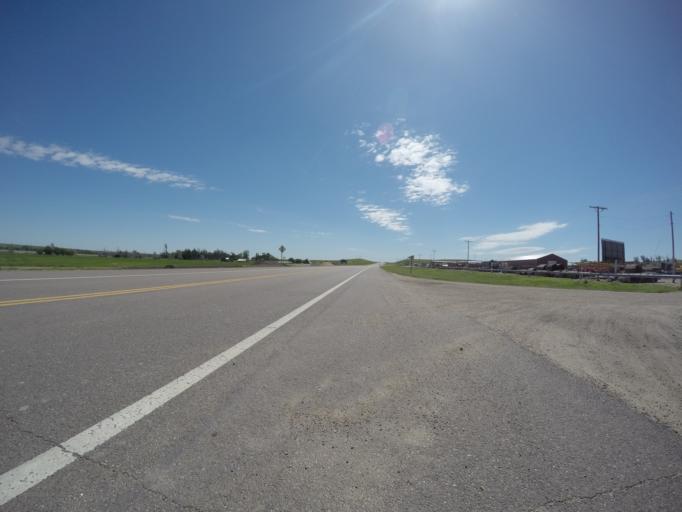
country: US
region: Kansas
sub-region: Rawlins County
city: Atwood
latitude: 39.8134
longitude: -101.0330
